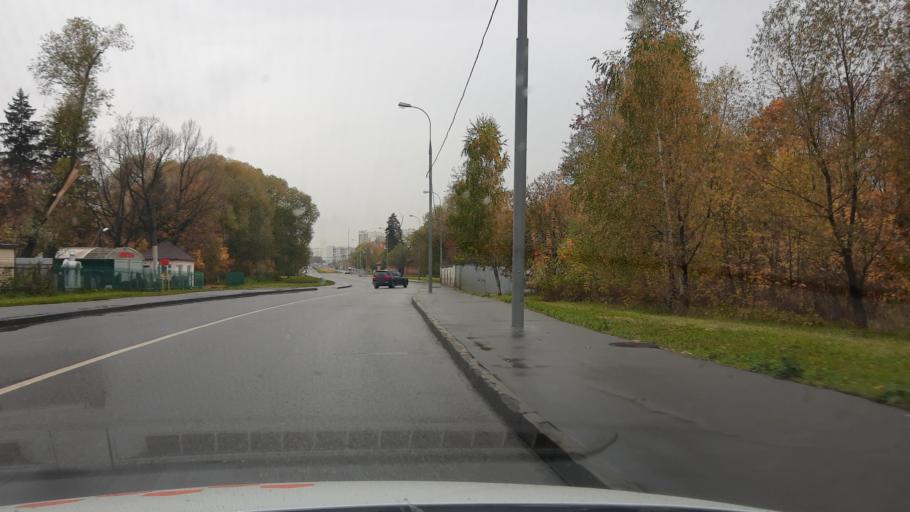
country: RU
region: Moskovskaya
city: Shcherbinka
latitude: 55.5394
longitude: 37.5627
